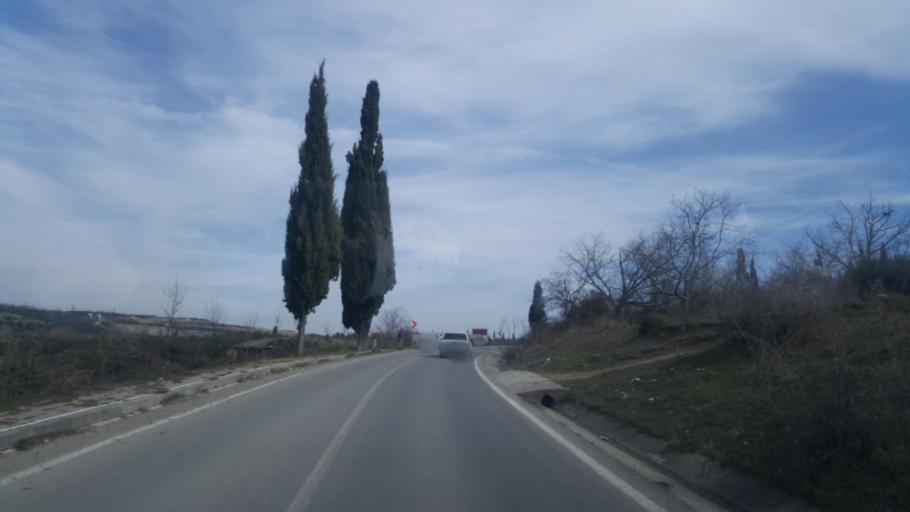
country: TR
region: Kocaeli
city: Tavsancil
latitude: 40.7887
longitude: 29.5702
